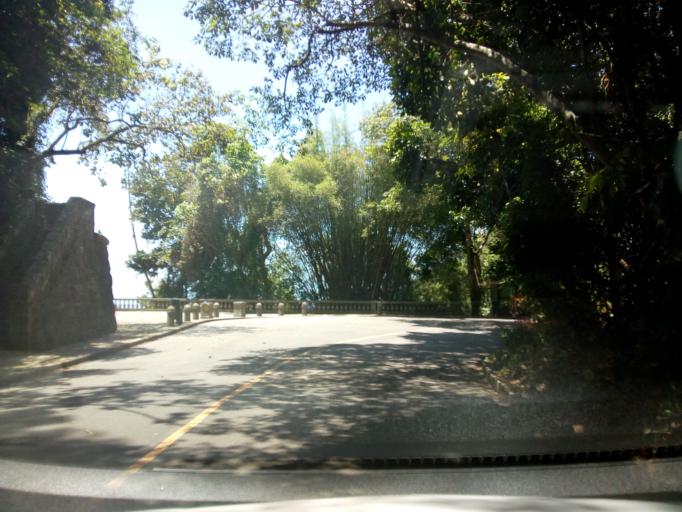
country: BR
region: Rio de Janeiro
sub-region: Rio De Janeiro
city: Rio de Janeiro
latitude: -22.9703
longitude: -43.2584
